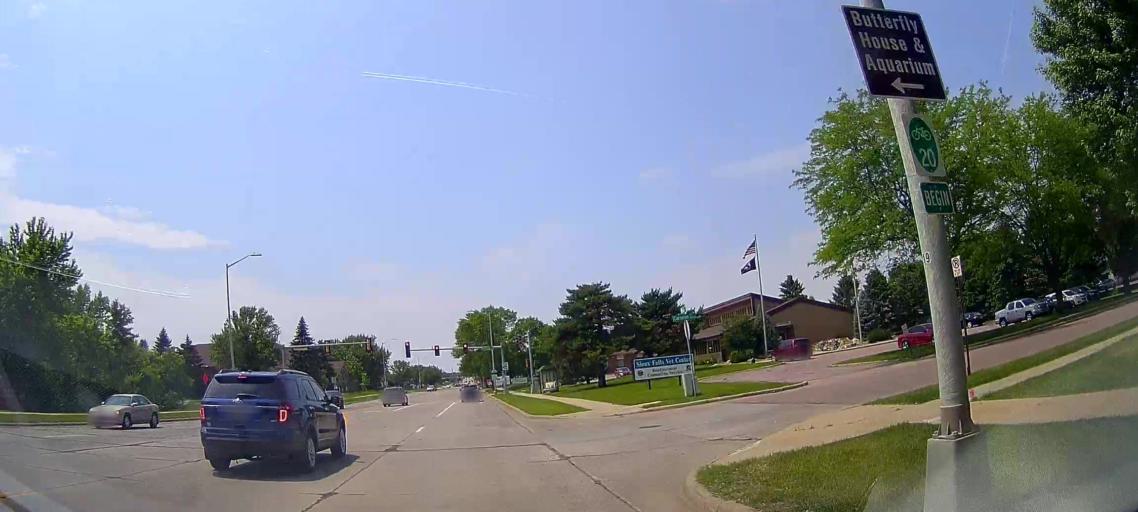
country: US
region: South Dakota
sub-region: Minnehaha County
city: Sioux Falls
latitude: 43.5077
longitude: -96.7651
